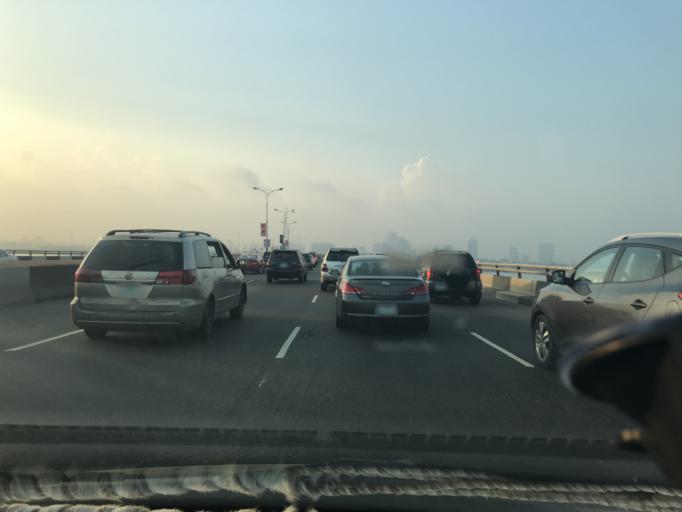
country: NG
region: Lagos
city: Ebute Metta
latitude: 6.4740
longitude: 3.3902
